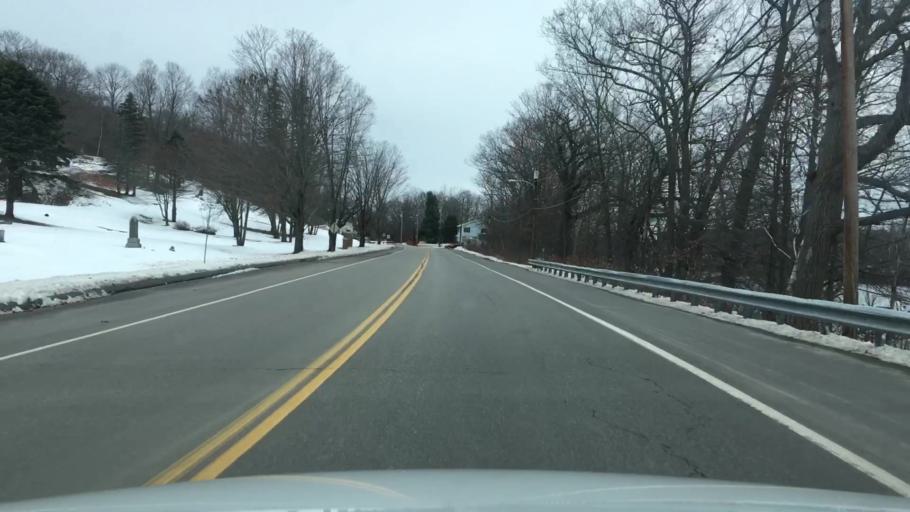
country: US
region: Maine
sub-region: Androscoggin County
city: Lewiston
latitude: 44.0807
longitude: -70.2112
